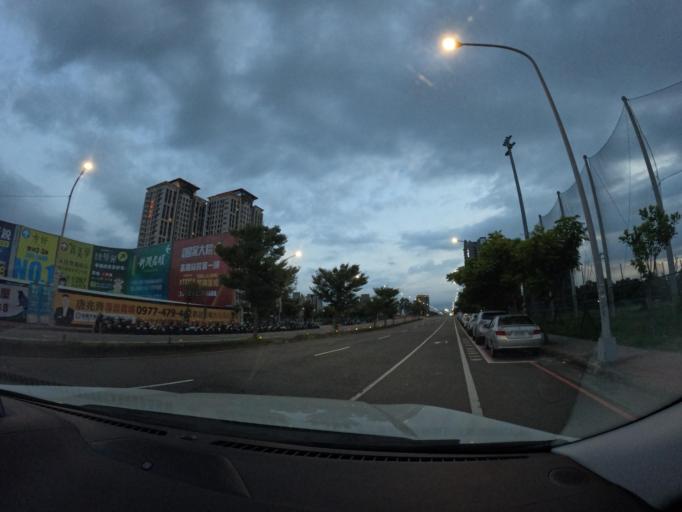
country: TW
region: Taiwan
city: Taoyuan City
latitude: 25.0128
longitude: 121.2112
